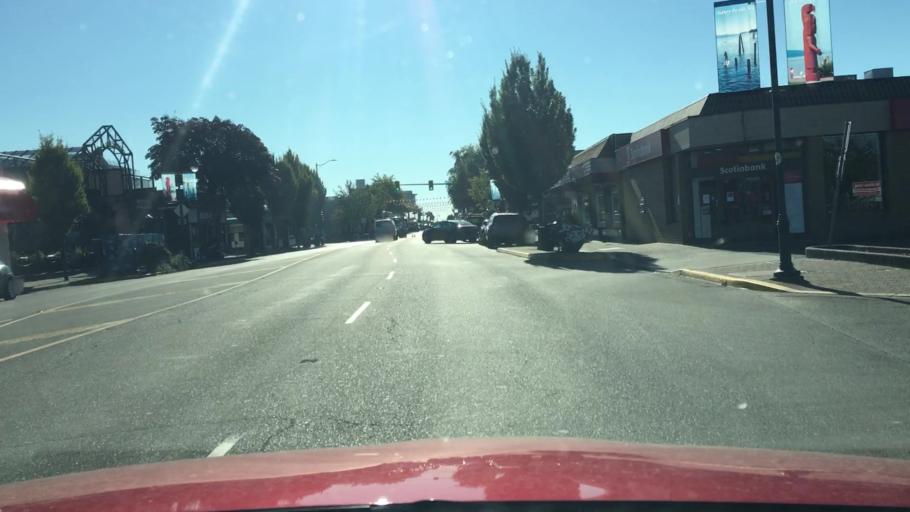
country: CA
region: British Columbia
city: North Saanich
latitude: 48.6489
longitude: -123.4018
